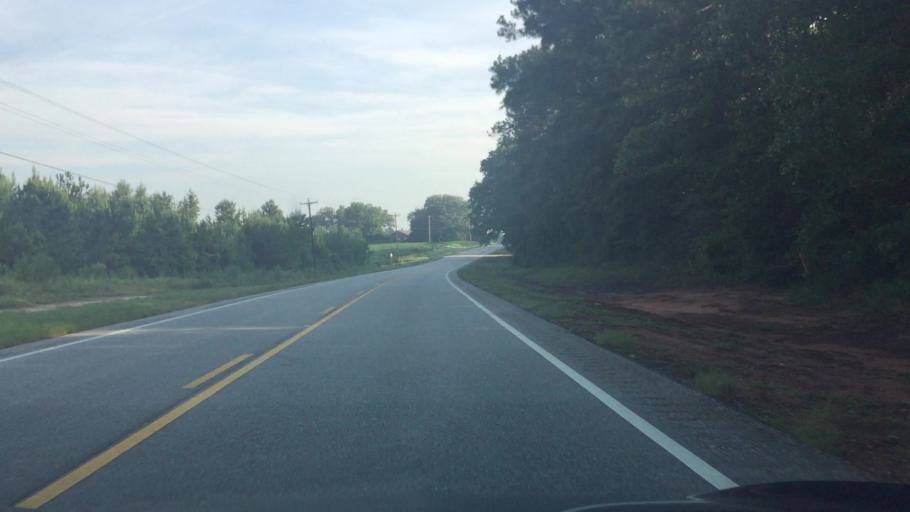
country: US
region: Alabama
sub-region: Covington County
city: Andalusia
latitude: 31.1666
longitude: -86.4600
